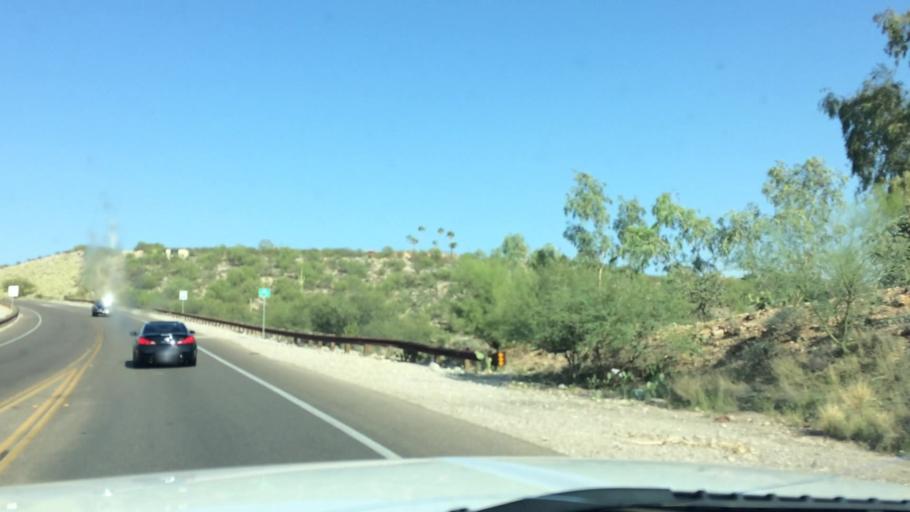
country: US
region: Arizona
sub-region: Pima County
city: Catalina Foothills
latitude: 32.3060
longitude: -110.8677
